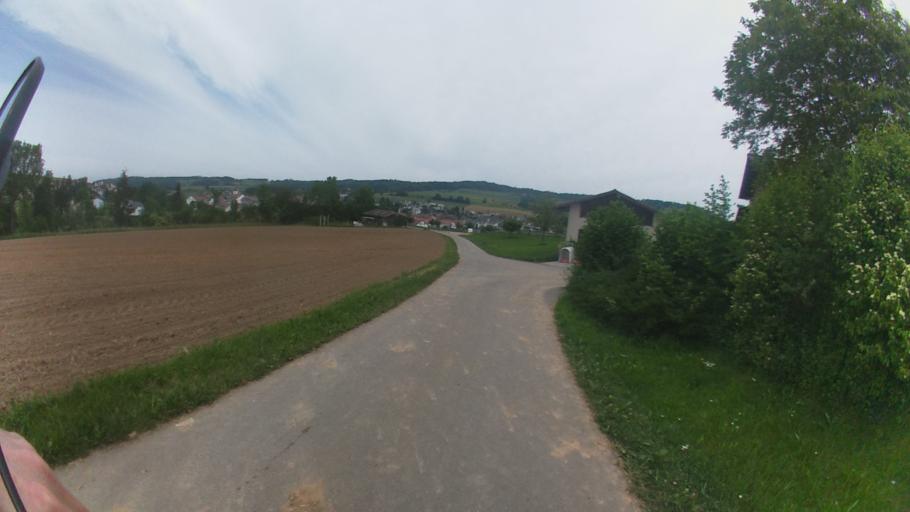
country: CH
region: Aargau
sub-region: Bezirk Baden
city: Unterehrendingen
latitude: 47.5154
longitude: 8.3308
